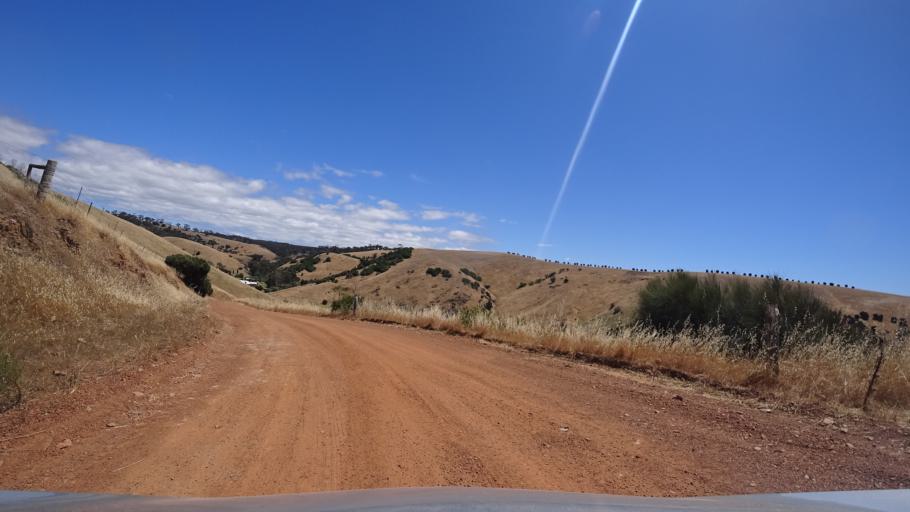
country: AU
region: South Australia
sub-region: Kangaroo Island
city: Kingscote
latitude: -35.6768
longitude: 136.9732
